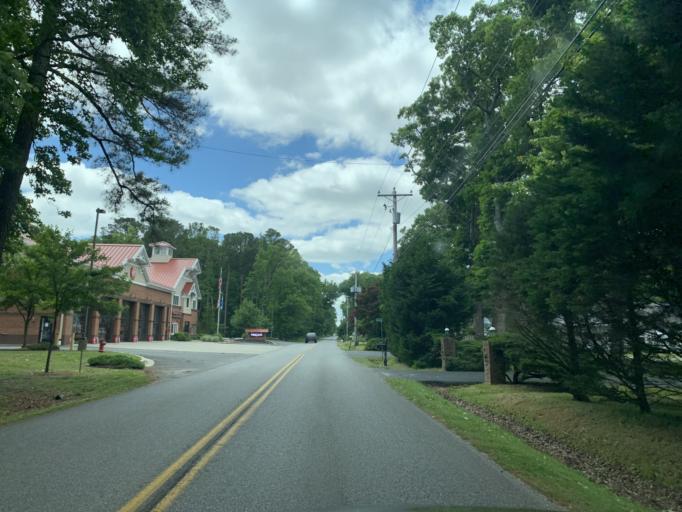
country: US
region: Maryland
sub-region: Worcester County
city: West Ocean City
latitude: 38.3460
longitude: -75.1166
